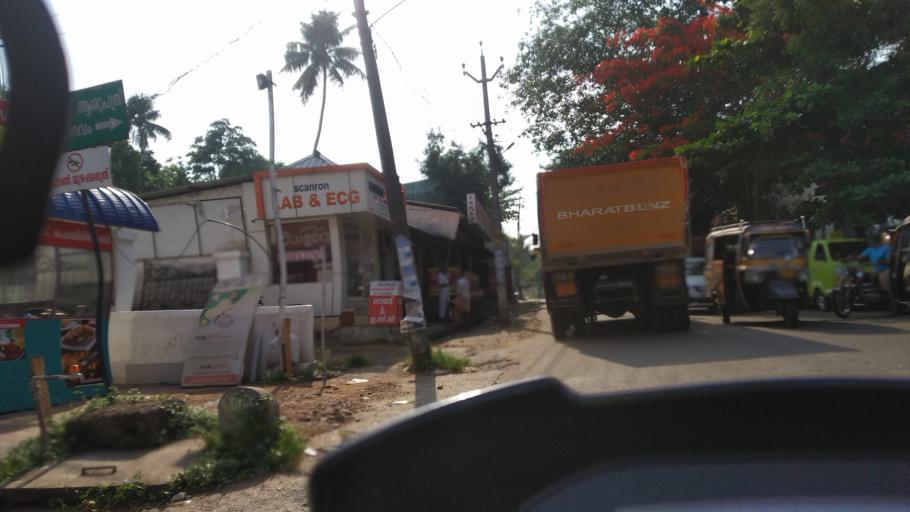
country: IN
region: Kerala
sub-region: Ernakulam
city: Piravam
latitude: 9.8741
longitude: 76.4949
